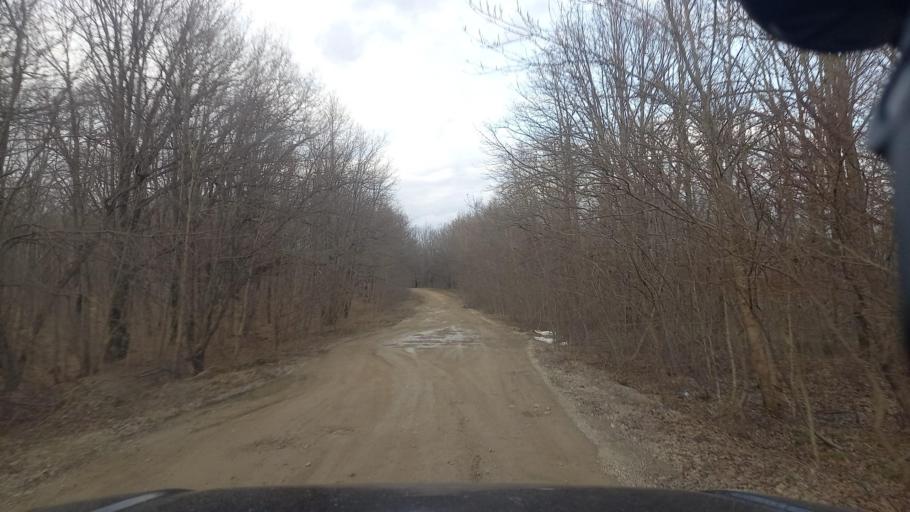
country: RU
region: Krasnodarskiy
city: Goryachiy Klyuch
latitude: 44.6907
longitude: 38.9843
